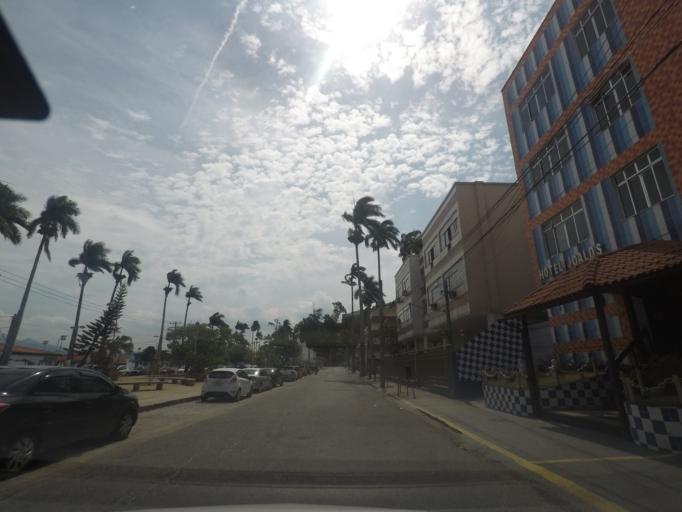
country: BR
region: Rio de Janeiro
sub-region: Rio De Janeiro
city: Rio de Janeiro
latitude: -22.8187
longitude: -43.2006
